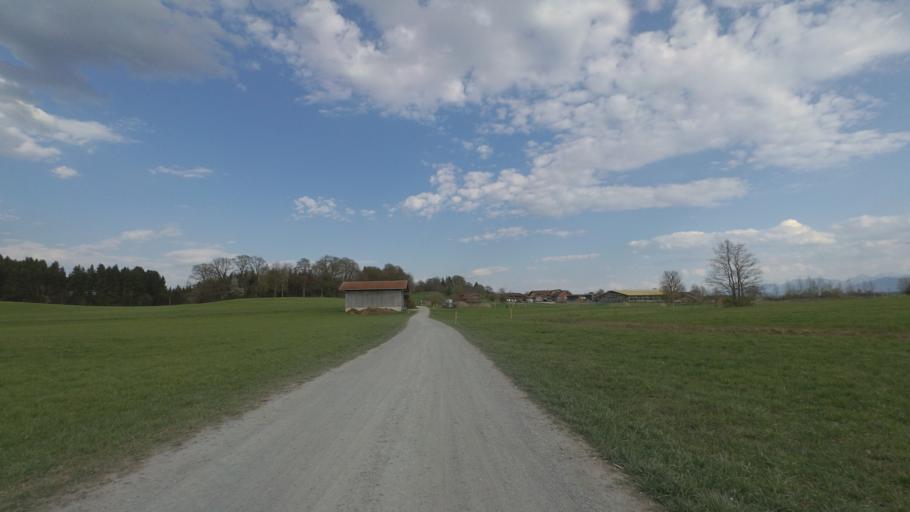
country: DE
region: Bavaria
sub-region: Upper Bavaria
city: Chieming
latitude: 47.9234
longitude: 12.5224
